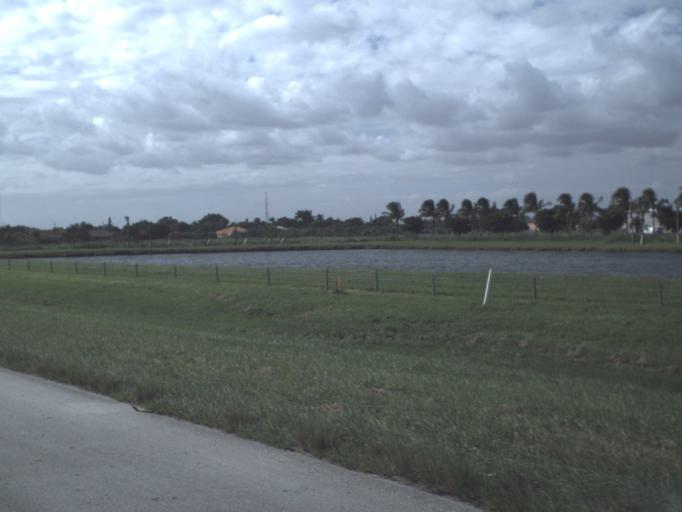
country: US
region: Florida
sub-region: Miami-Dade County
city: Princeton
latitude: 25.5303
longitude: -80.3841
